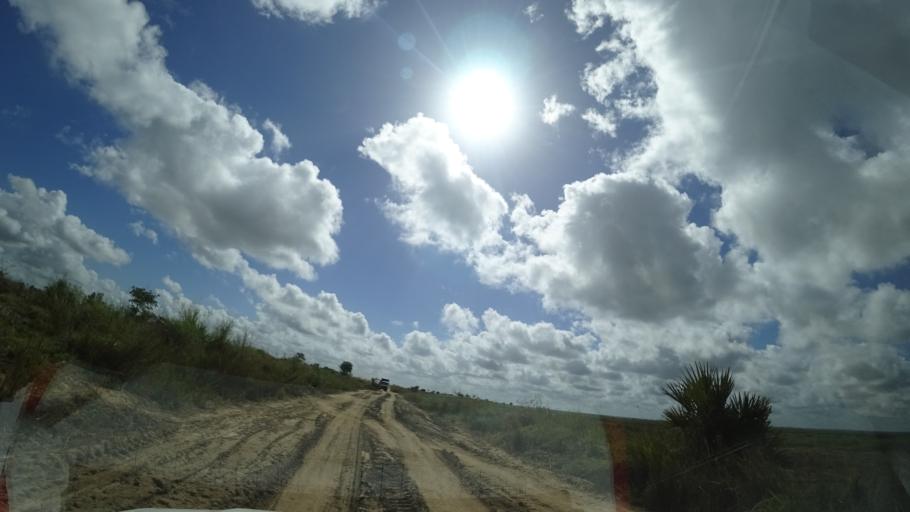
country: MZ
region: Sofala
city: Dondo
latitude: -19.4217
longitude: 34.5633
